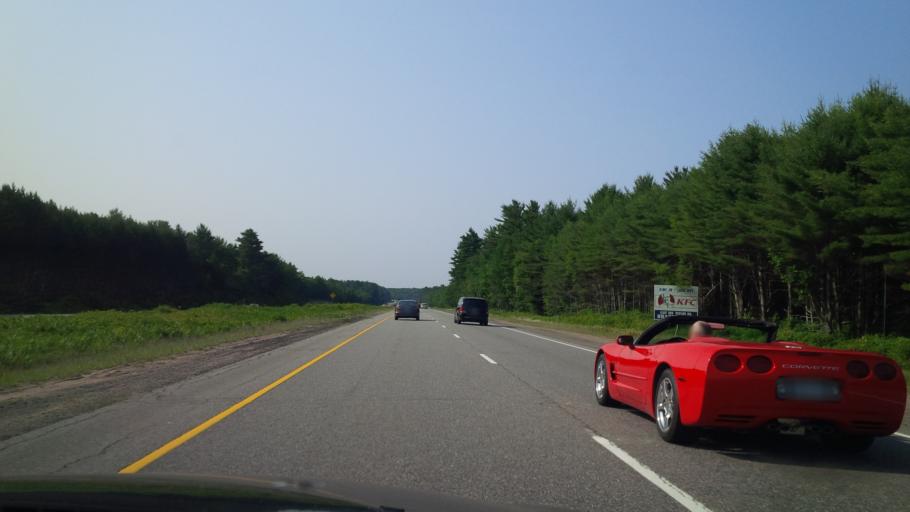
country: CA
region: Ontario
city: Bracebridge
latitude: 45.1247
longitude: -79.3111
